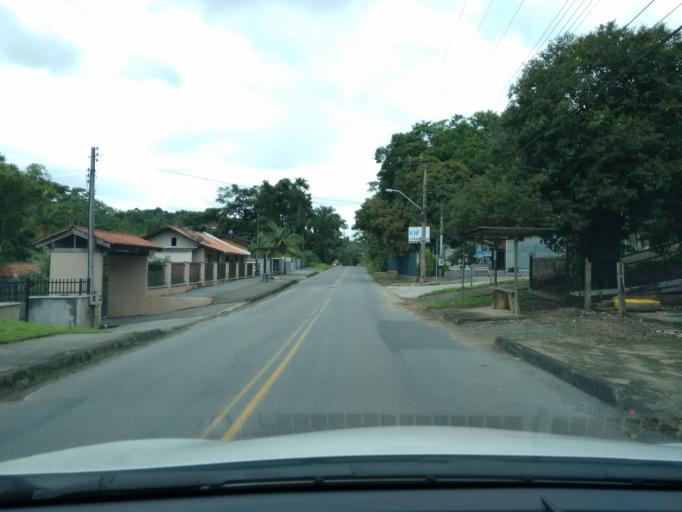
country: BR
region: Santa Catarina
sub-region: Blumenau
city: Blumenau
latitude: -26.8642
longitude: -49.1390
